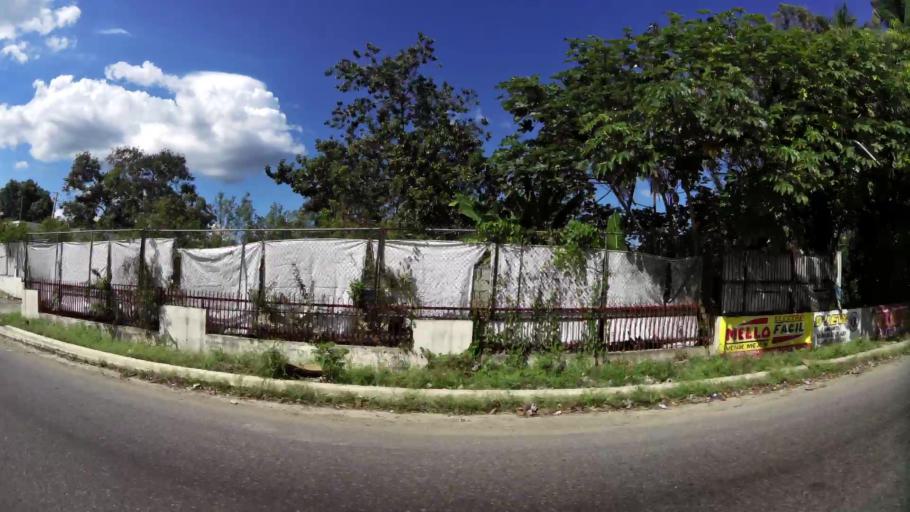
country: DO
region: San Cristobal
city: San Cristobal
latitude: 18.4249
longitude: -70.0705
